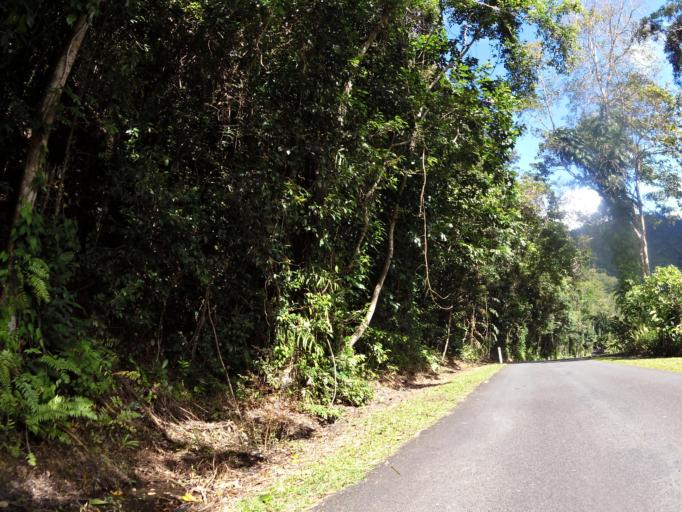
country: AU
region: Queensland
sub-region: Cairns
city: Woree
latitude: -16.9587
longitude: 145.6834
